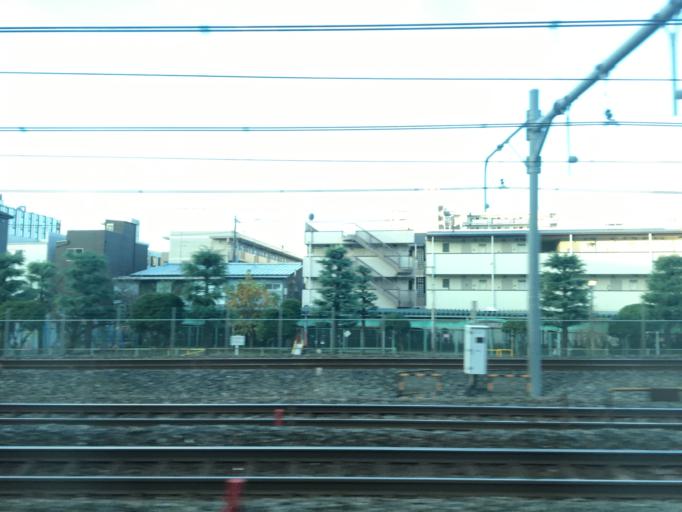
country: JP
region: Saitama
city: Yono
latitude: 35.8742
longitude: 139.6439
